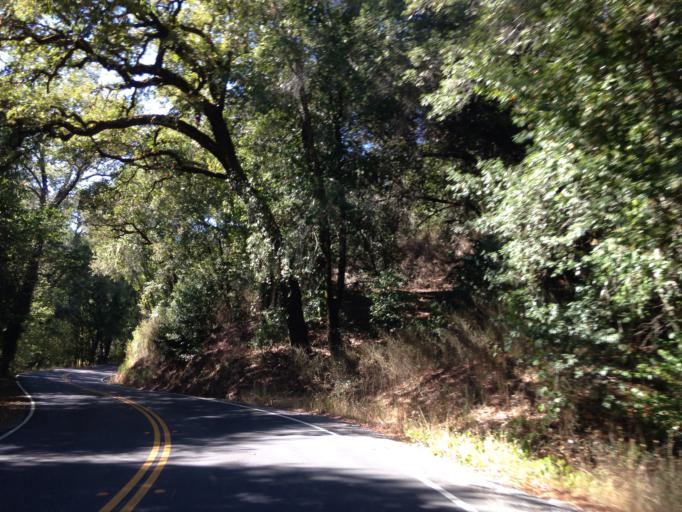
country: US
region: California
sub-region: Sonoma County
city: Forestville
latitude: 38.5101
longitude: -122.9109
